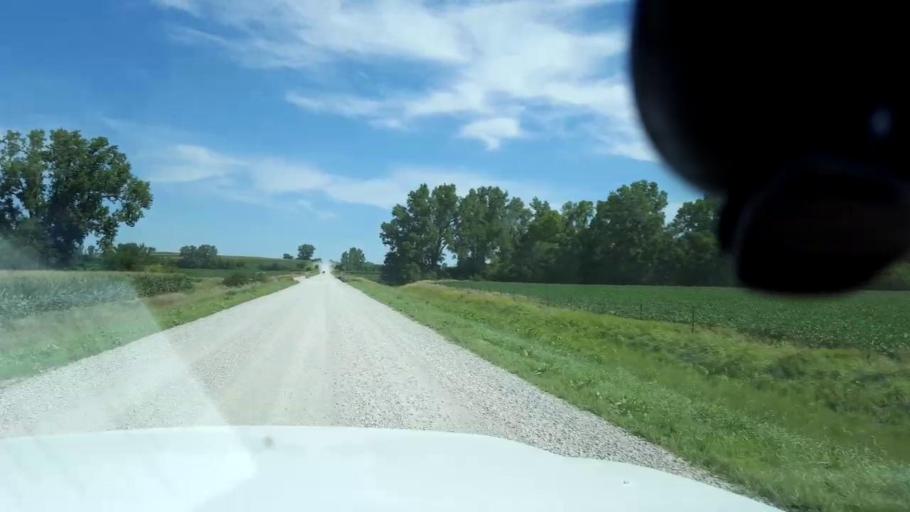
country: US
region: Iowa
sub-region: Pottawattamie County
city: Oakland
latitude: 41.2479
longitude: -95.5371
